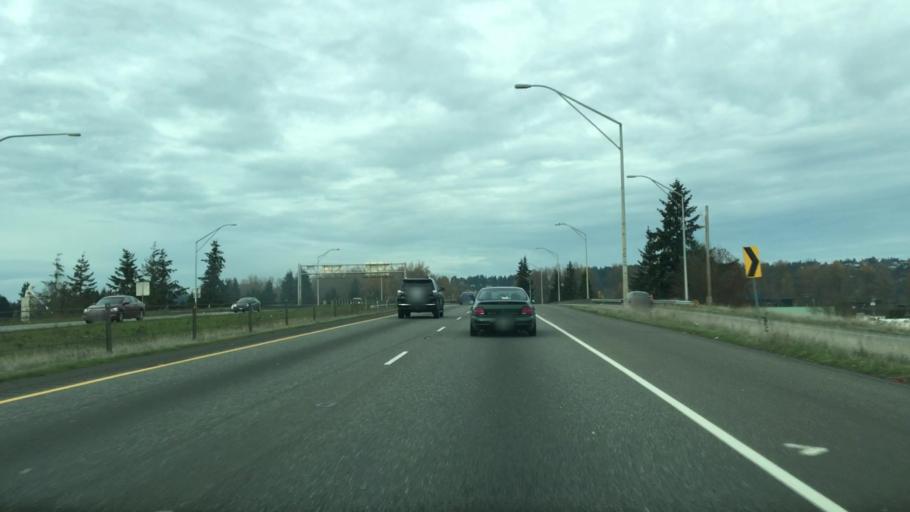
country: US
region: Washington
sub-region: Pierce County
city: Puyallup
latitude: 47.1888
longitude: -122.2827
